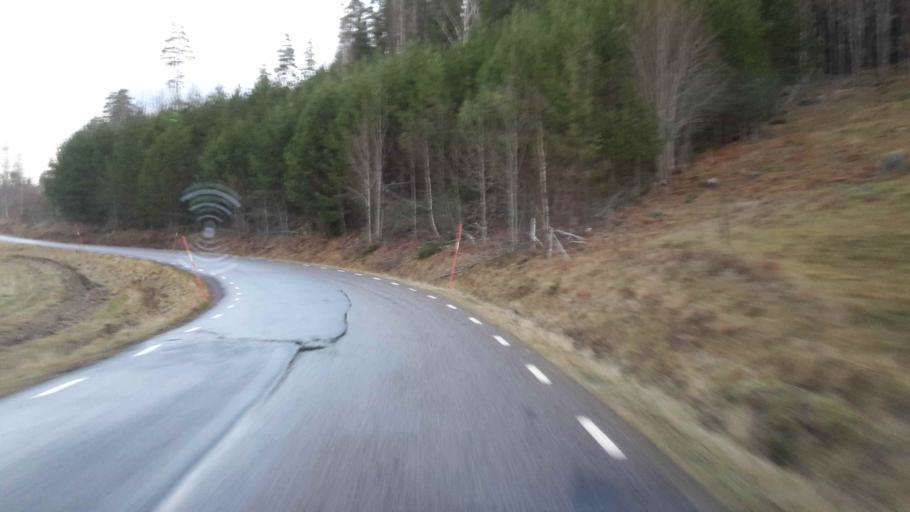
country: SE
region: Kalmar
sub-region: Vasterviks Kommun
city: Overum
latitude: 58.1620
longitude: 16.3322
